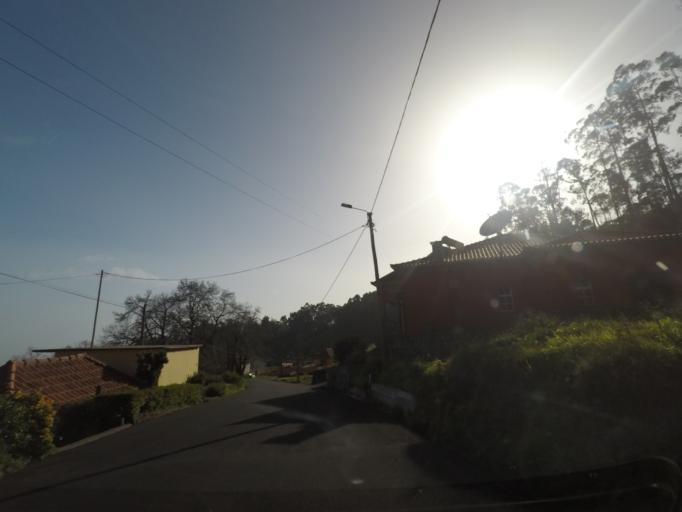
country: PT
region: Madeira
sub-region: Ribeira Brava
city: Campanario
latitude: 32.6810
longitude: -17.0077
